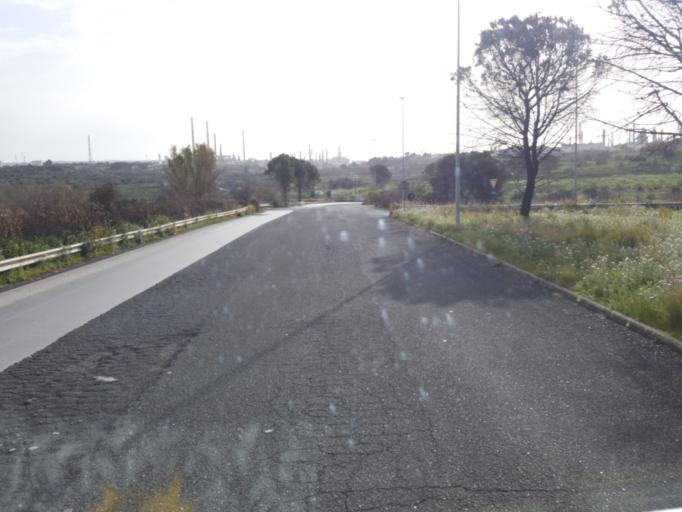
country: IT
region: Sicily
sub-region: Provincia di Siracusa
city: Melilli
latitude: 37.2181
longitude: 15.1516
